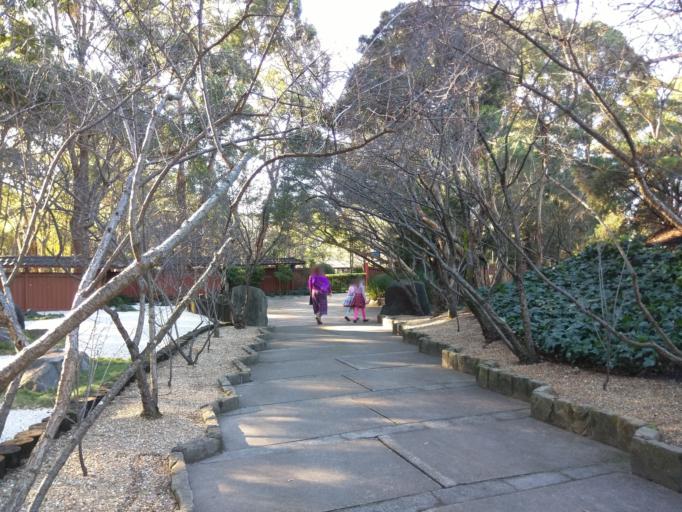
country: AU
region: New South Wales
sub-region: Auburn
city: Auburn
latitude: -33.8590
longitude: 151.0174
